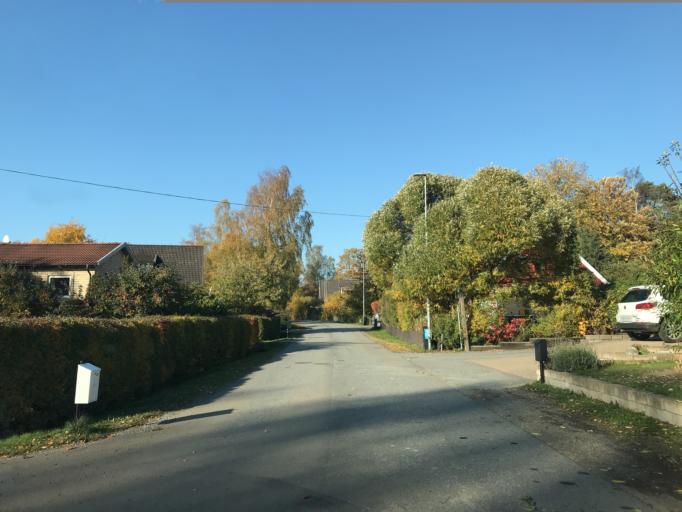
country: SE
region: Stockholm
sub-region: Sollentuna Kommun
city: Sollentuna
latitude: 59.4245
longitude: 17.9338
